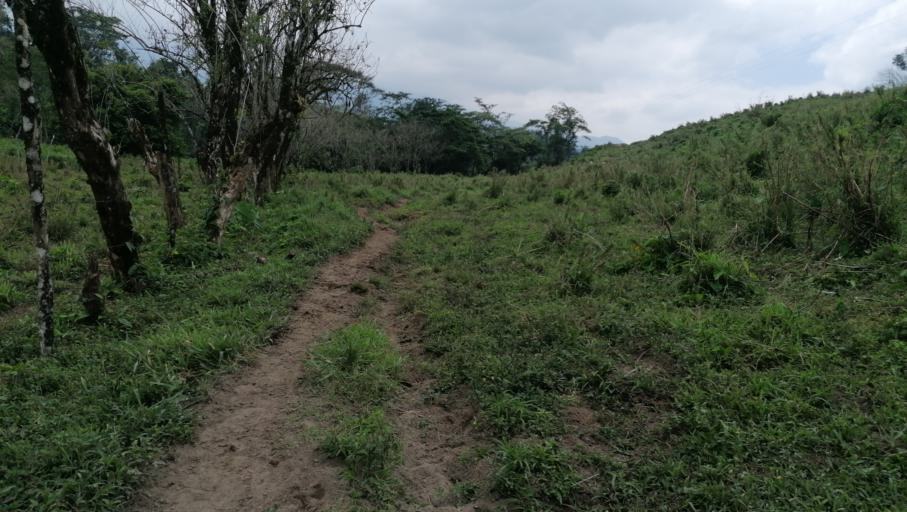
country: MX
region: Chiapas
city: Ocotepec
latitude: 17.3000
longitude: -93.2266
